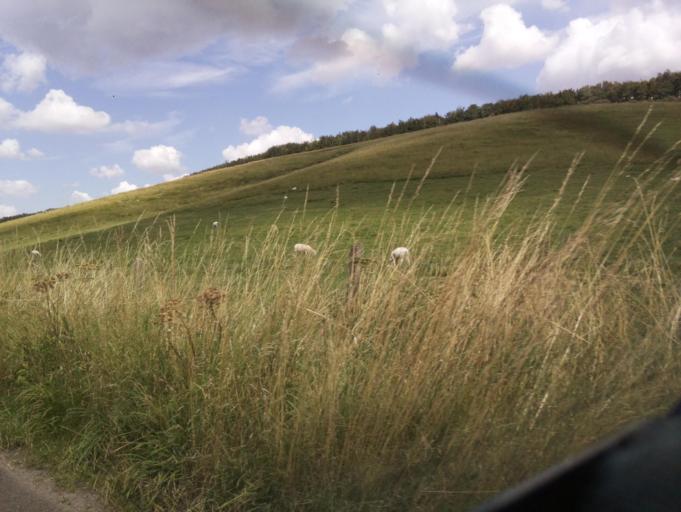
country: GB
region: England
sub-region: Borough of Swindon
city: Bishopstone
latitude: 51.5453
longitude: -1.5949
